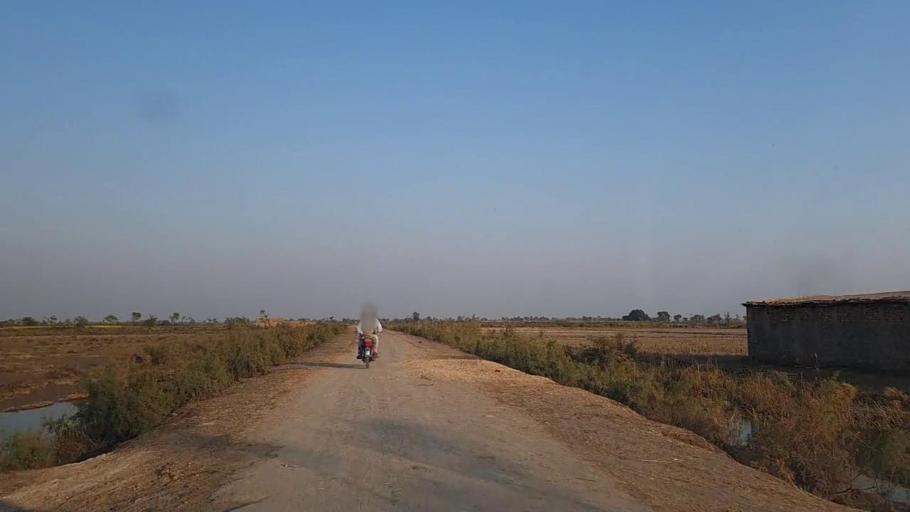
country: PK
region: Sindh
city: Bandhi
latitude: 26.5427
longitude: 68.3114
